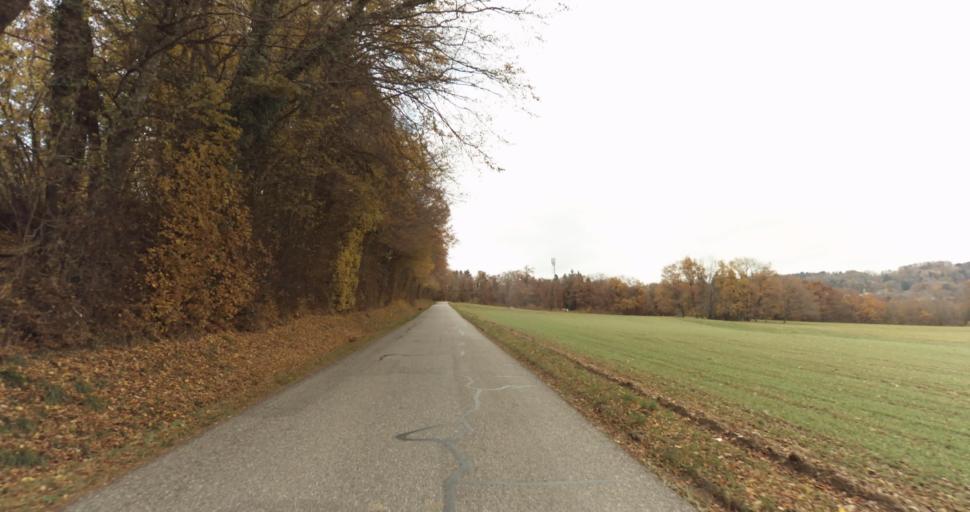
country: FR
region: Rhone-Alpes
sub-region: Departement de la Haute-Savoie
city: Pringy
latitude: 45.9639
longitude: 6.1215
